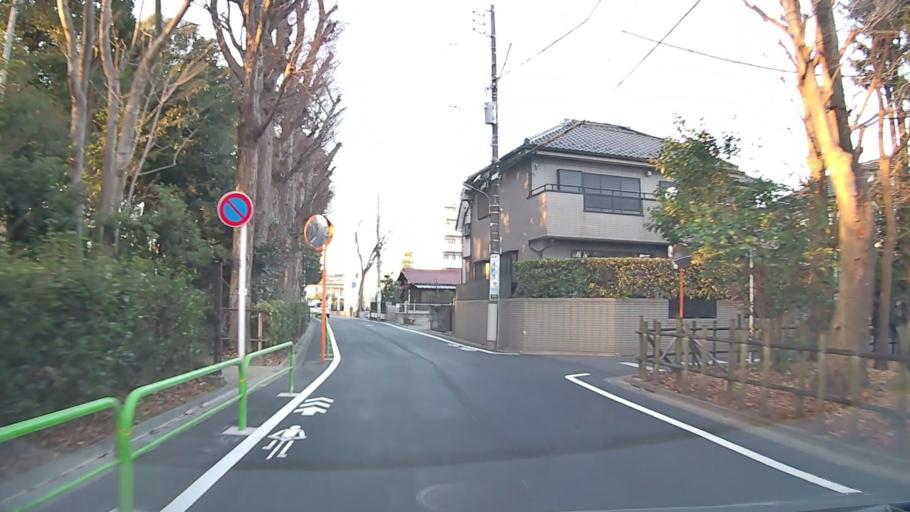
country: JP
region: Tokyo
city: Musashino
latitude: 35.7368
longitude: 139.5828
